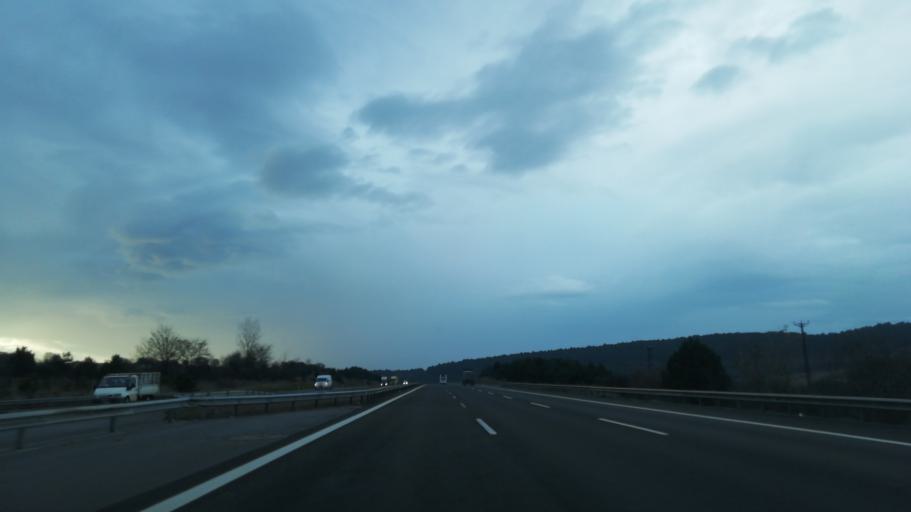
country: TR
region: Bolu
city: Yenicaga
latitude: 40.7526
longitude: 31.9256
